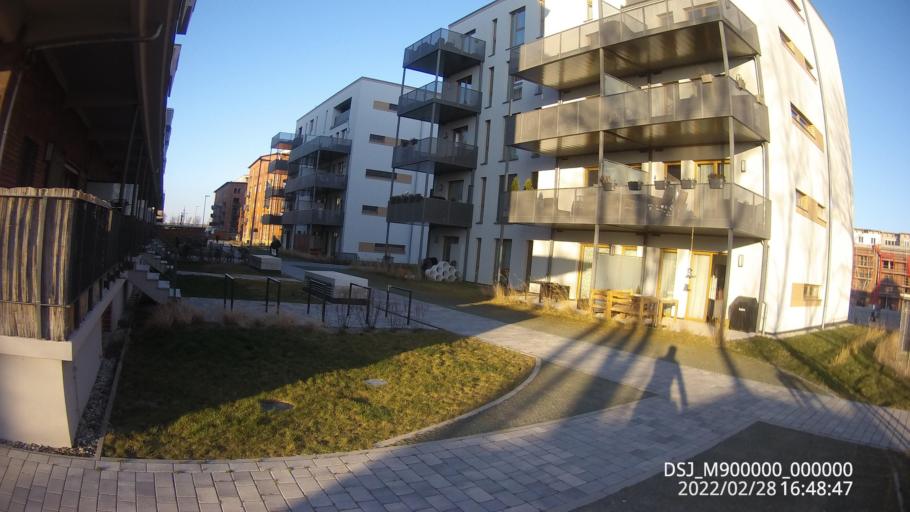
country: DE
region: Saxony
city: Leipzig
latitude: 51.3714
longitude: 12.3518
